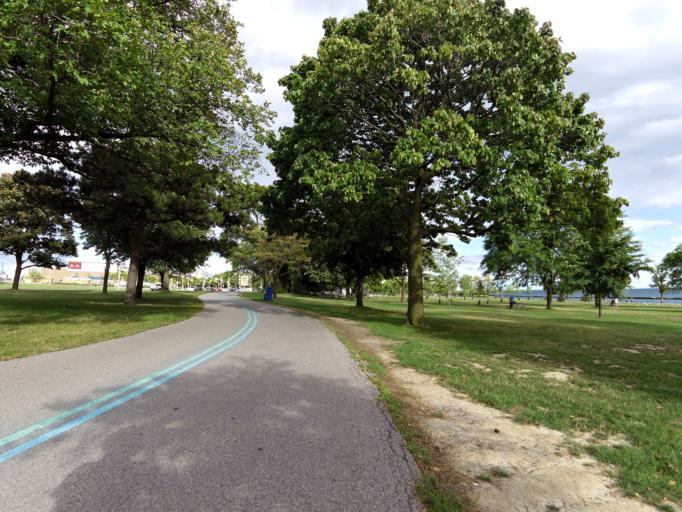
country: CA
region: Ontario
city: Toronto
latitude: 43.6313
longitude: -79.4314
